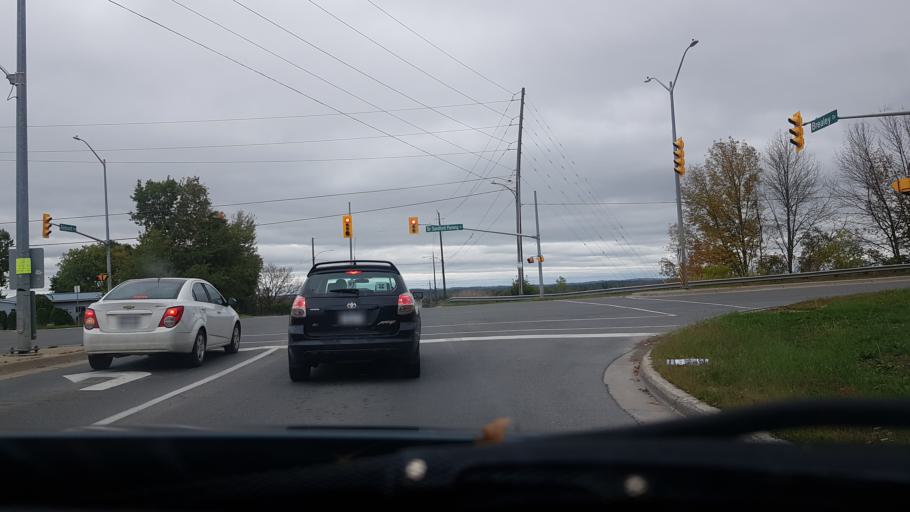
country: CA
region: Ontario
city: Peterborough
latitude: 44.2641
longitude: -78.3667
